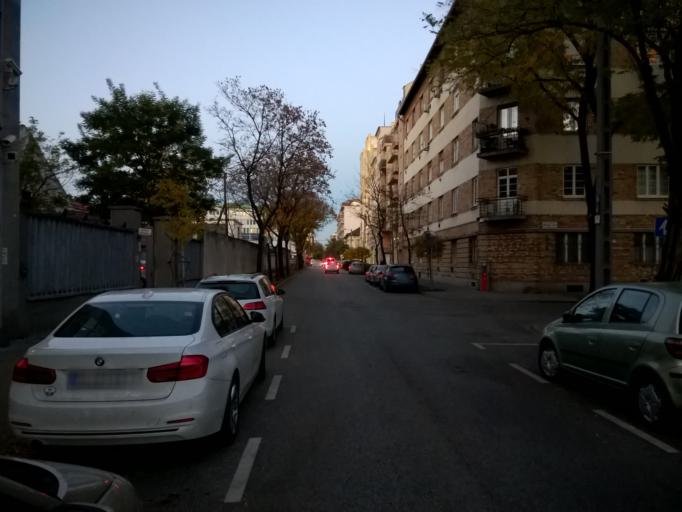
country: HU
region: Budapest
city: Budapest XIII. keruelet
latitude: 47.5260
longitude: 19.0743
